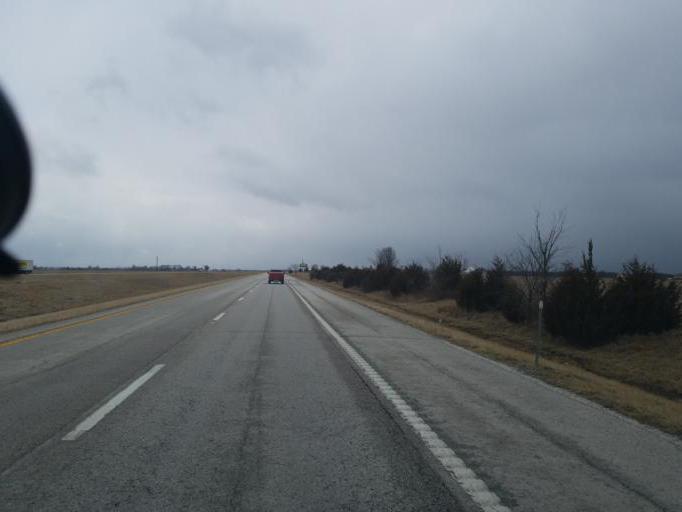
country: US
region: Missouri
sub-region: Randolph County
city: Moberly
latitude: 39.5086
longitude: -92.4344
